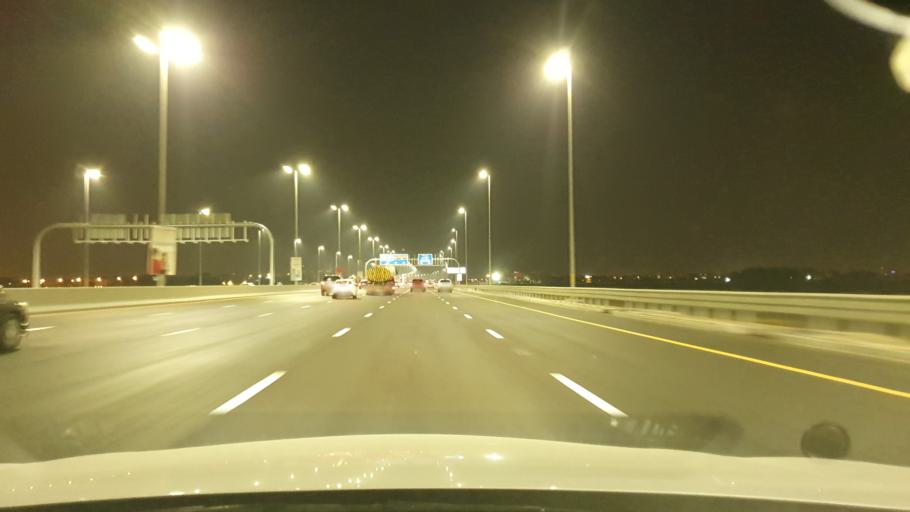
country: BH
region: Manama
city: Jidd Hafs
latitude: 26.2052
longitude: 50.5144
